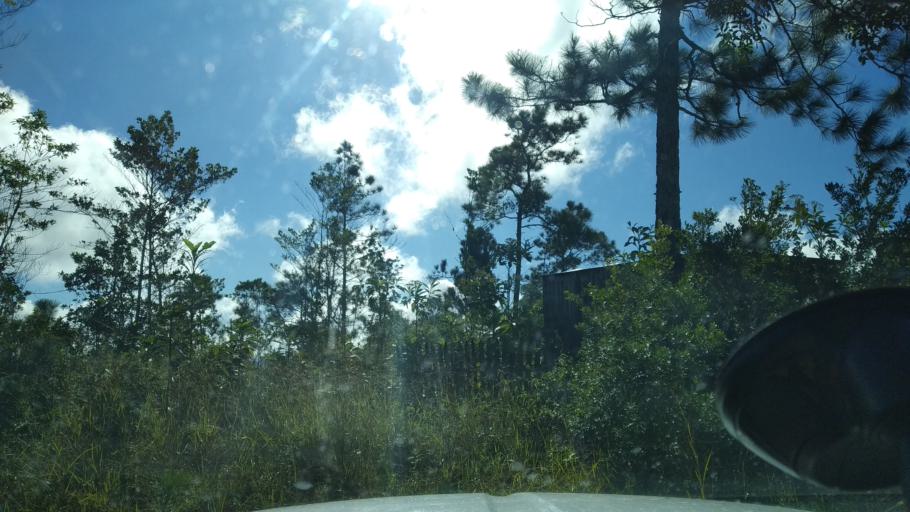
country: BZ
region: Cayo
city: Belmopan
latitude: 16.9988
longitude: -88.8480
